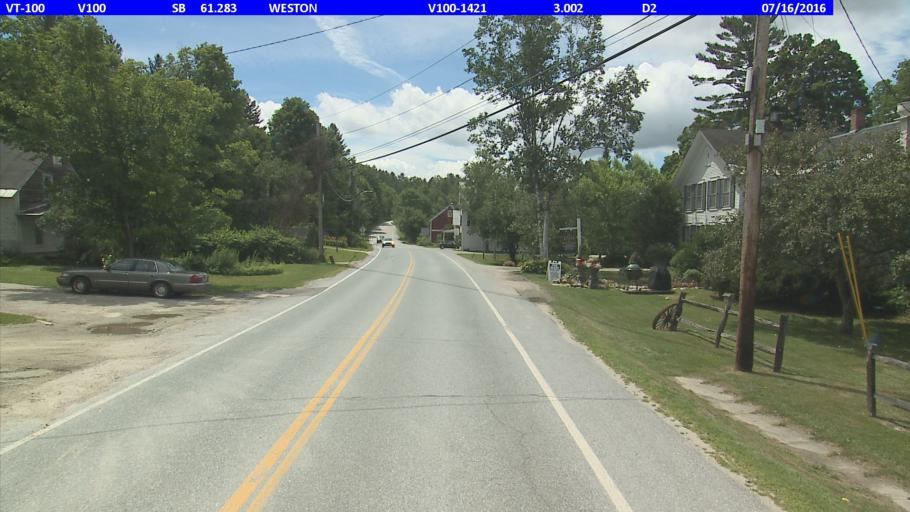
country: US
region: Vermont
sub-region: Windsor County
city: Chester
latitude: 43.2890
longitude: -72.7932
